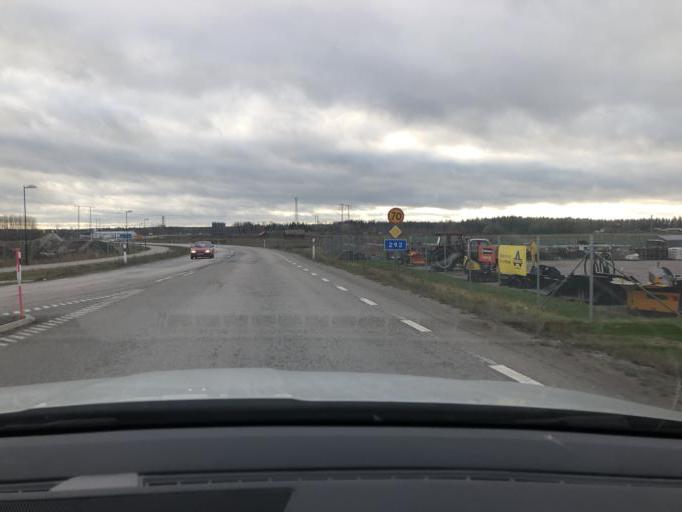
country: SE
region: Uppsala
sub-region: Tierps Kommun
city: Tierp
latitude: 60.3459
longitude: 17.4908
